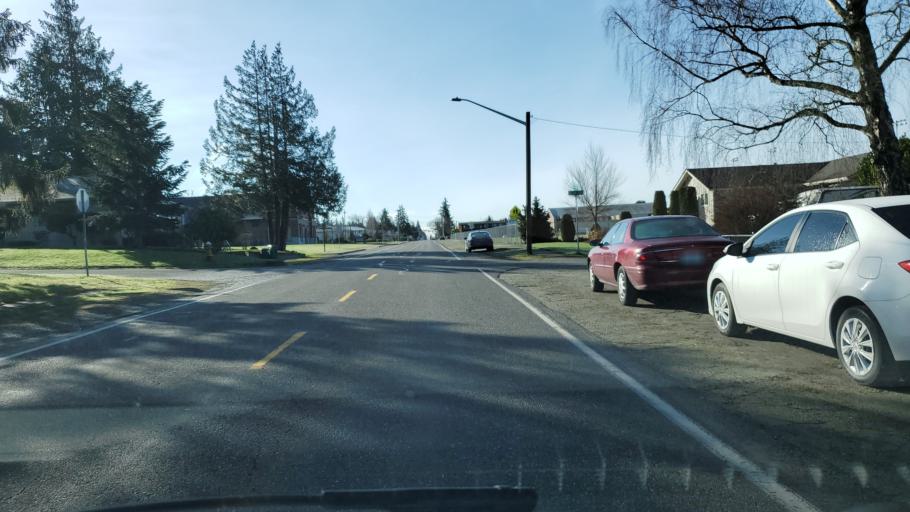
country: US
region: Washington
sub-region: Skagit County
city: Mount Vernon
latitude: 48.4253
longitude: -122.3230
